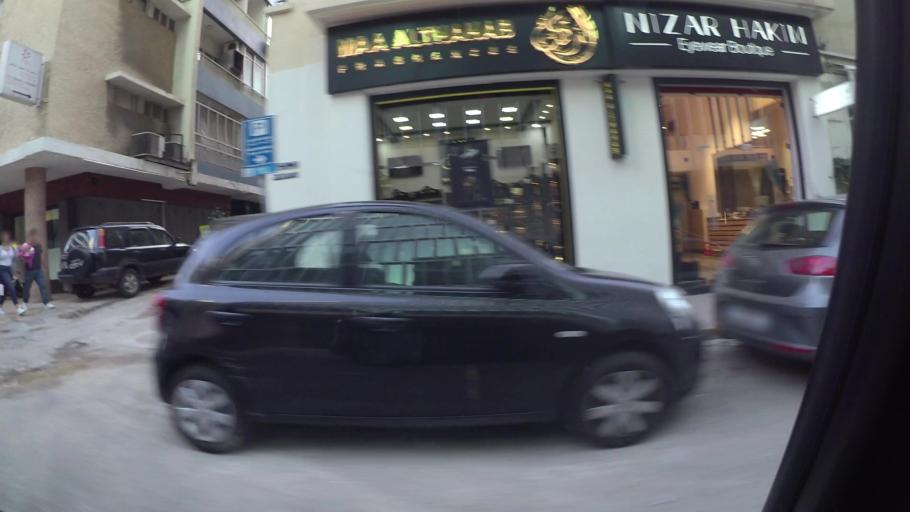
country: LB
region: Beyrouth
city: Ra's Bayrut
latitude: 33.8977
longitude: 35.4839
